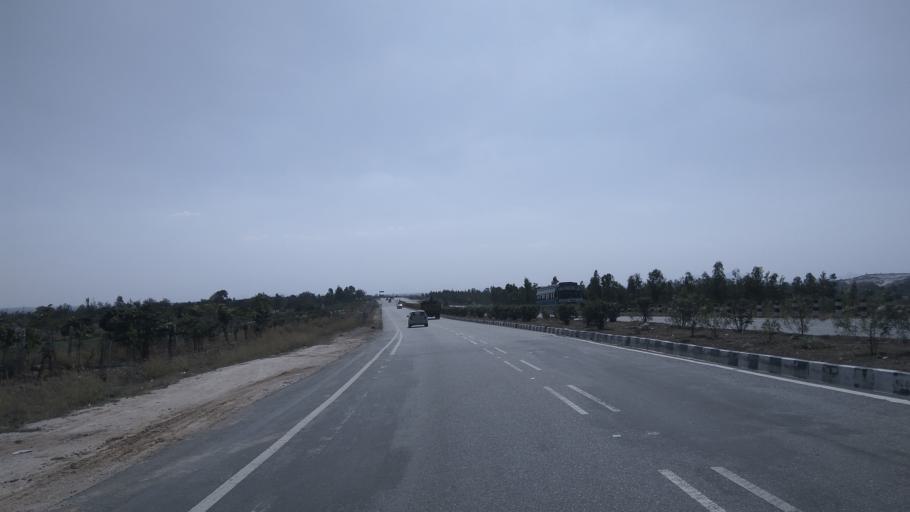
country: IN
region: Karnataka
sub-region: Kolar
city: Mulbagal
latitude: 13.1539
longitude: 78.3066
